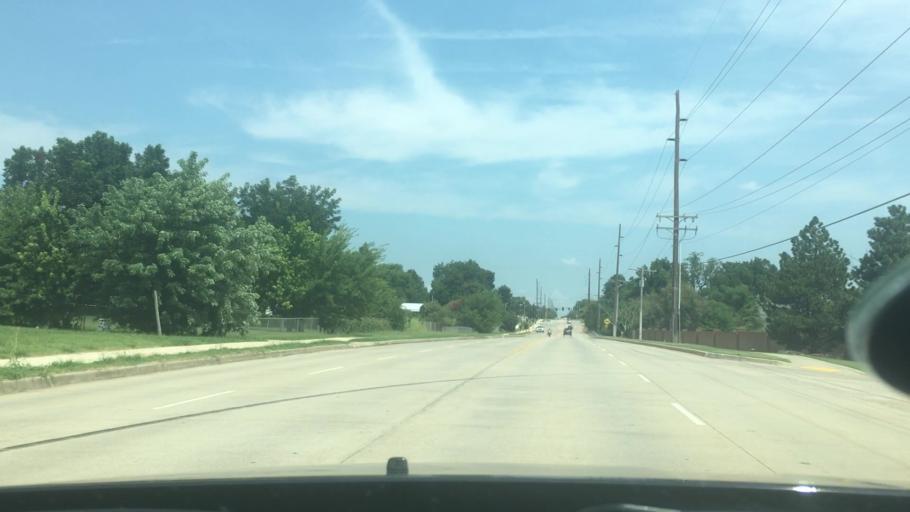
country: US
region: Oklahoma
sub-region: Pottawatomie County
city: Shawnee
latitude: 35.3432
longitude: -96.8943
